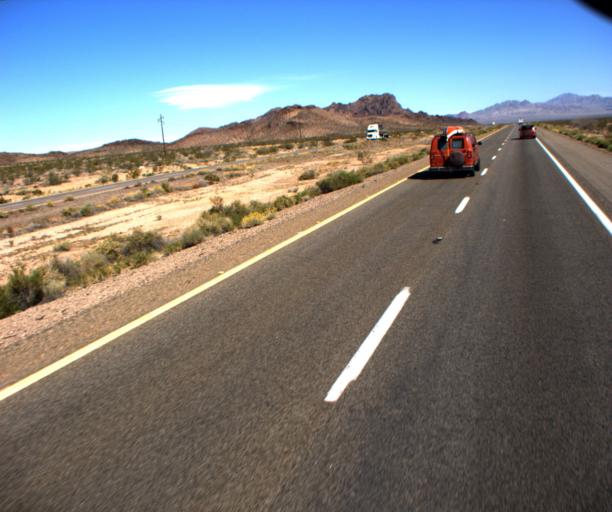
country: US
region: Arizona
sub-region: Mohave County
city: Dolan Springs
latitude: 35.7559
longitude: -114.5046
